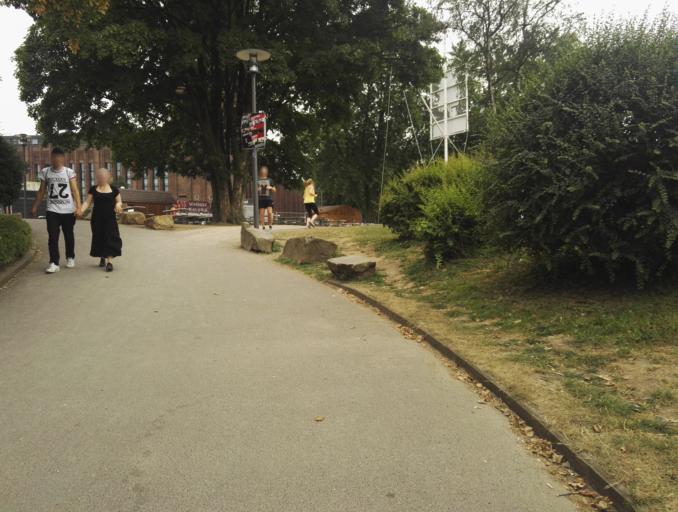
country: DE
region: North Rhine-Westphalia
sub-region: Regierungsbezirk Koln
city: Deutz
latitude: 50.9452
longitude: 6.9697
